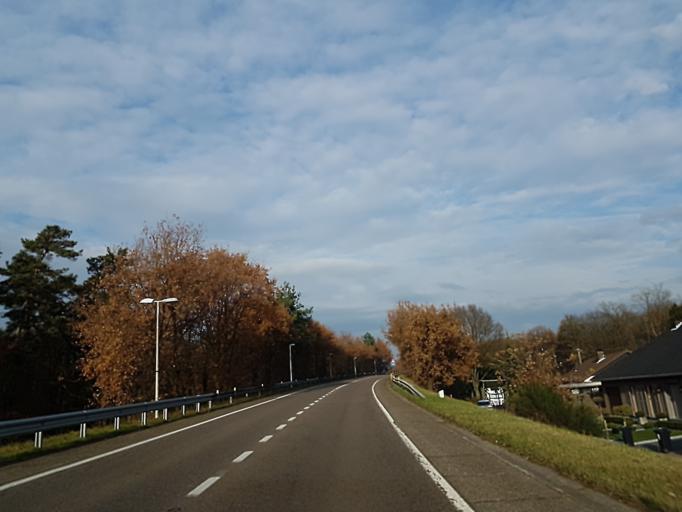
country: BE
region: Flanders
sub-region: Provincie Antwerpen
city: Essen
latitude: 51.4316
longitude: 4.4612
